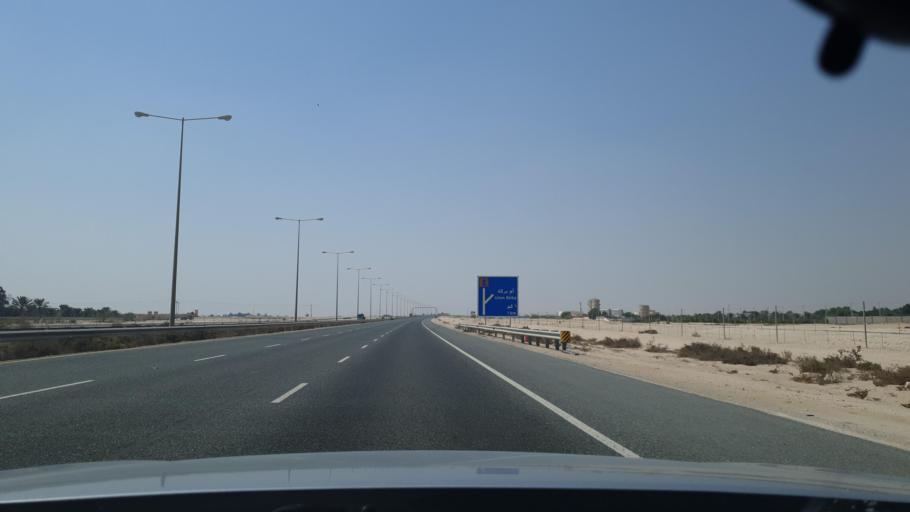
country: QA
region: Al Khawr
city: Al Khawr
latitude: 25.7549
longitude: 51.4500
